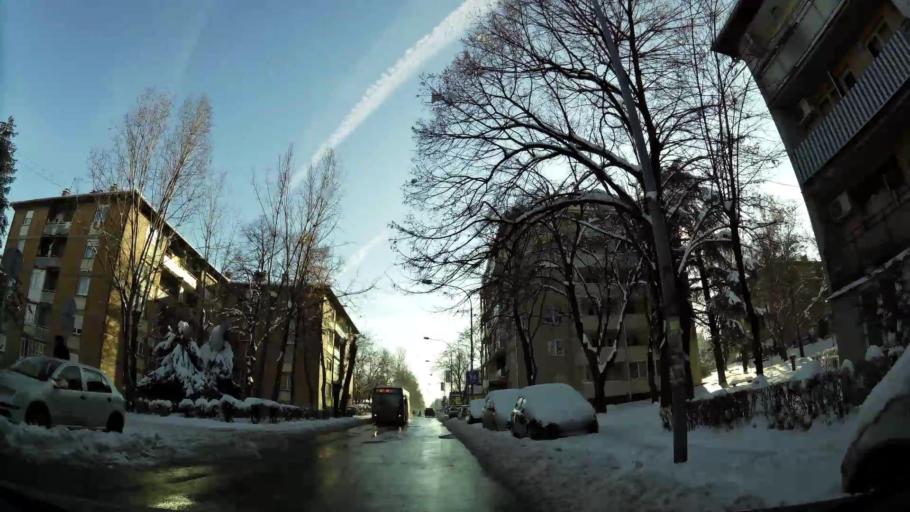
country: RS
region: Central Serbia
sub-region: Belgrade
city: Palilula
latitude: 44.8097
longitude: 20.5219
